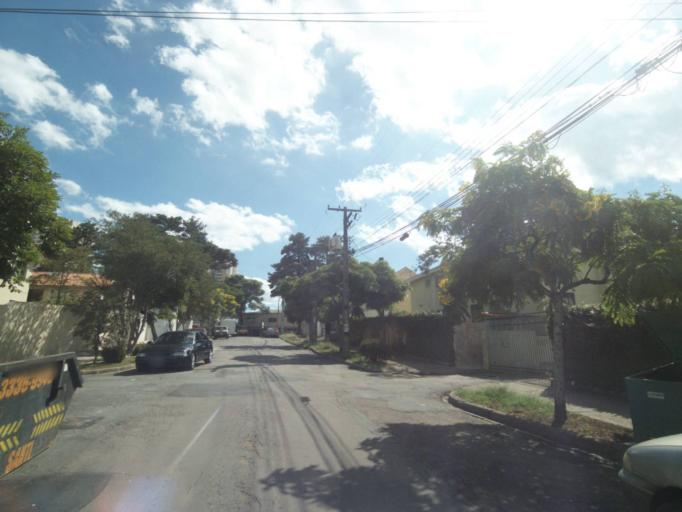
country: BR
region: Parana
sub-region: Curitiba
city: Curitiba
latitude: -25.4382
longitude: -49.3465
